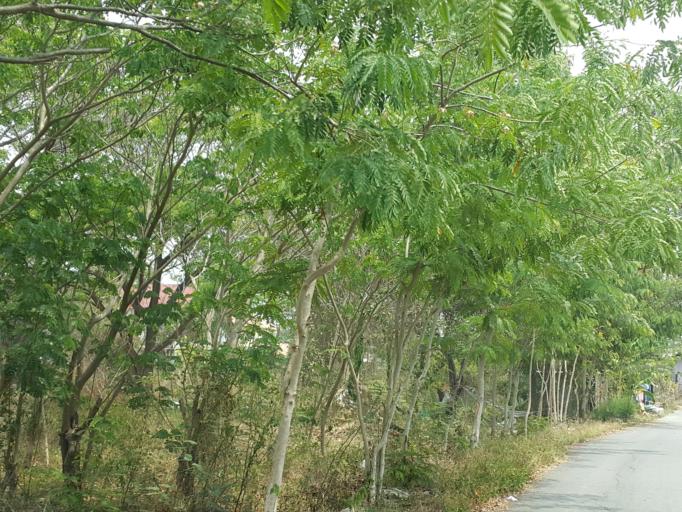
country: TH
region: Chiang Mai
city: Saraphi
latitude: 18.7493
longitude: 99.0373
